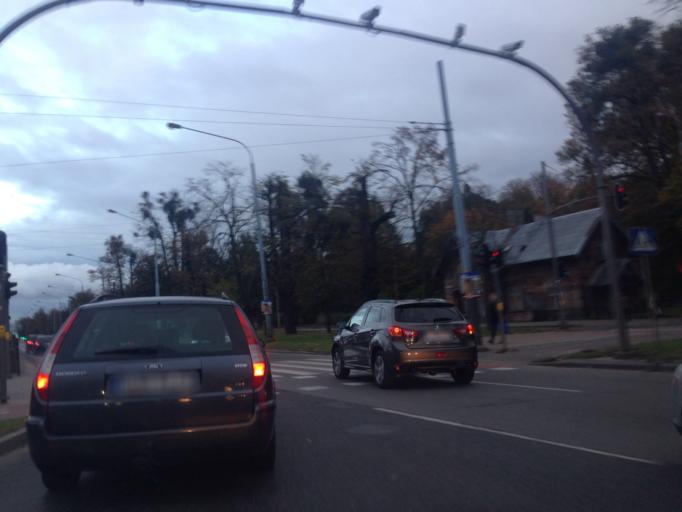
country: PL
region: Pomeranian Voivodeship
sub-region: Gdansk
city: Gdansk
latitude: 54.3723
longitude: 18.6242
